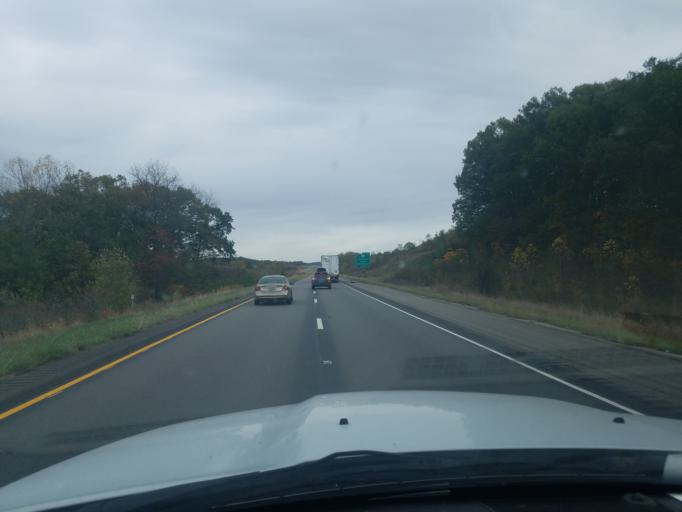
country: US
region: Indiana
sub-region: Dubois County
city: Ferdinand
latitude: 38.2069
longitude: -86.8865
